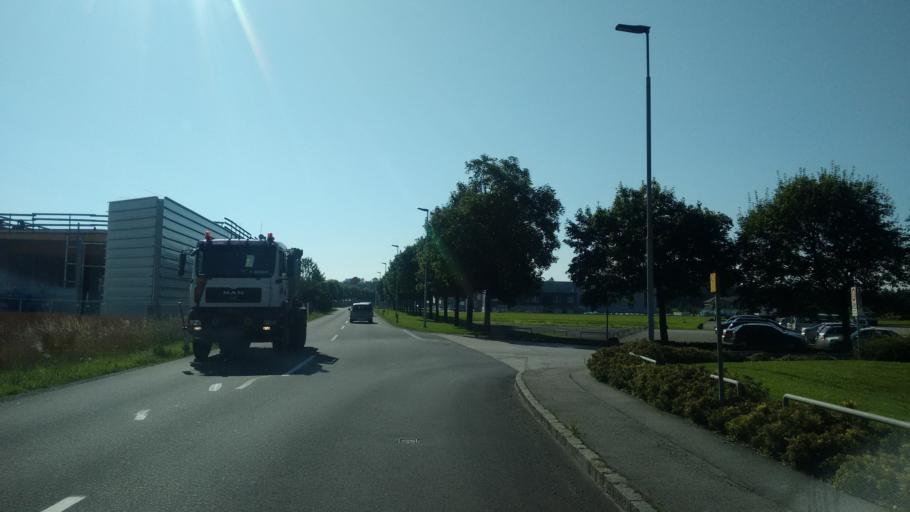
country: AT
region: Upper Austria
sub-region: Wels-Land
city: Gunskirchen
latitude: 48.1338
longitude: 13.9530
